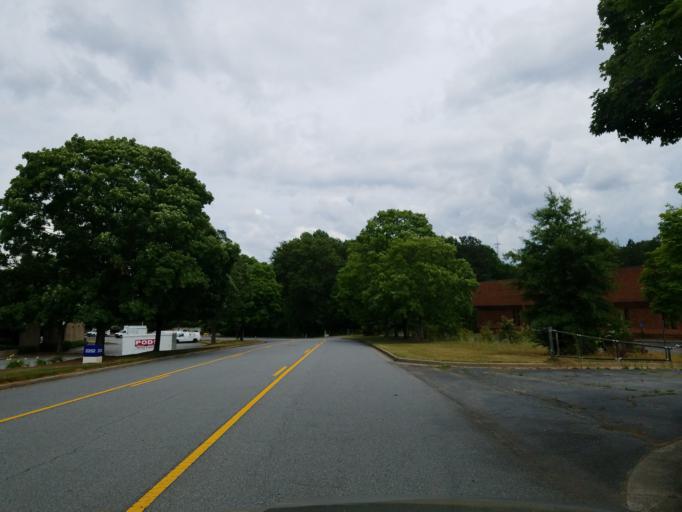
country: US
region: Georgia
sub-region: Cobb County
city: Smyrna
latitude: 33.9183
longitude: -84.4890
